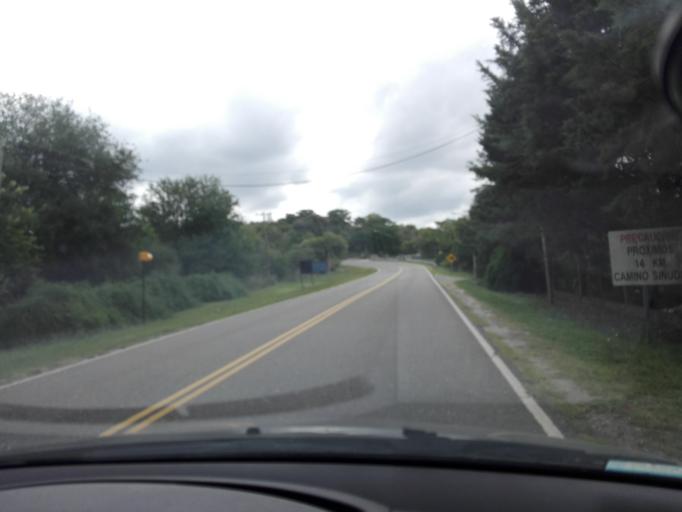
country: AR
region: Cordoba
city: Alta Gracia
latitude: -31.5865
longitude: -64.4614
